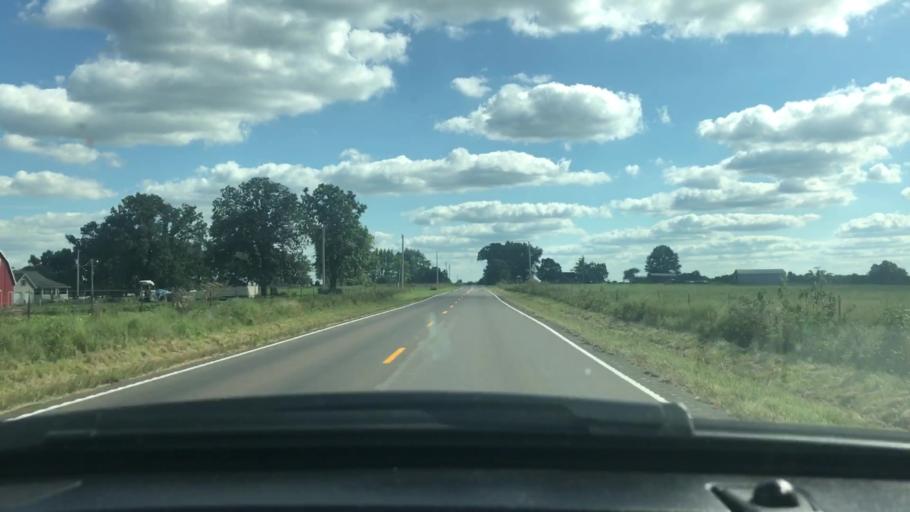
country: US
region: Missouri
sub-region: Wright County
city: Mountain Grove
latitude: 37.2655
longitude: -92.3081
